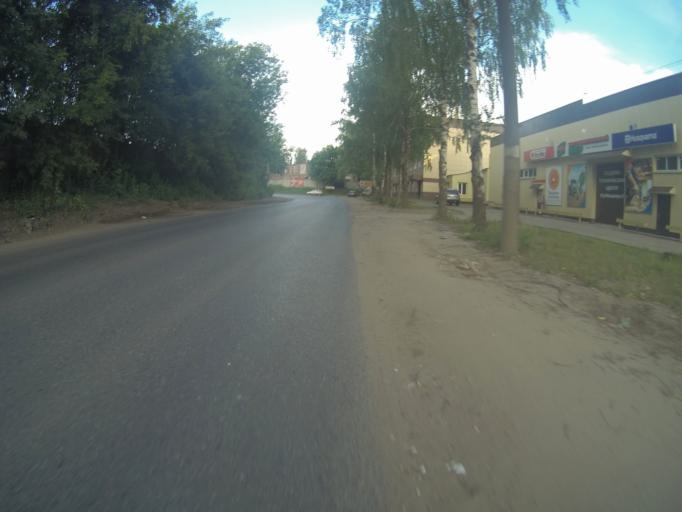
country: RU
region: Vladimir
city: Vladimir
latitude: 56.1601
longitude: 40.3816
